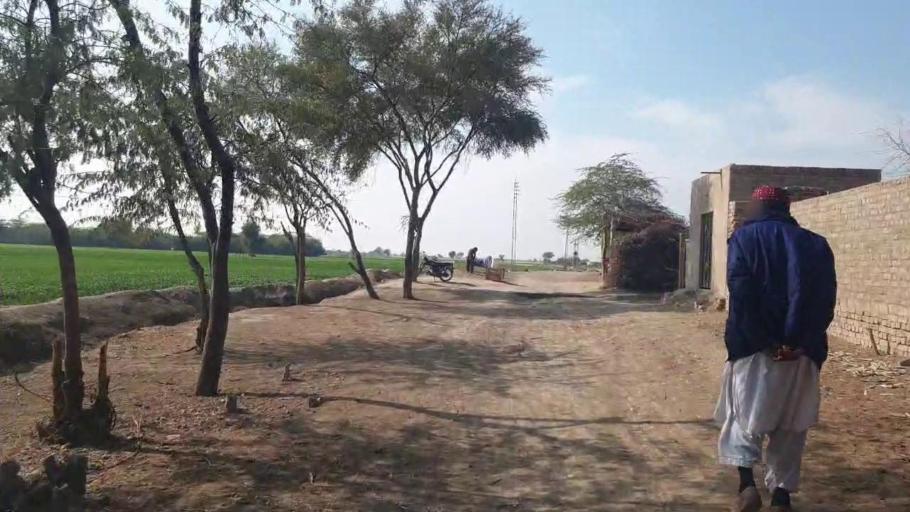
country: PK
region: Sindh
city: Shahdadpur
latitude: 25.9900
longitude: 68.5629
